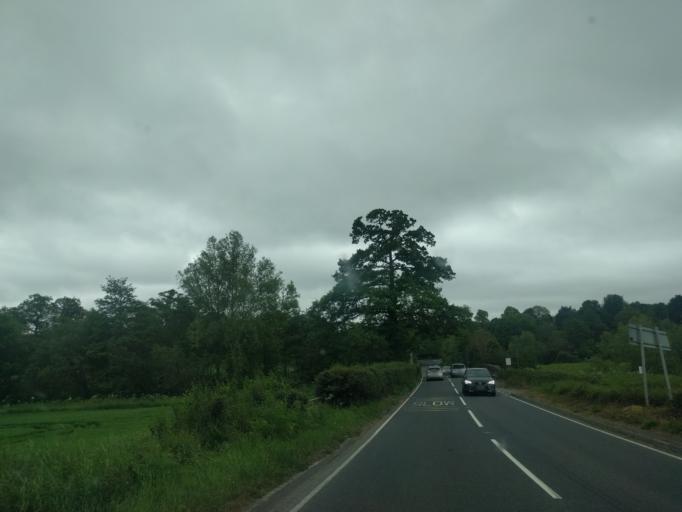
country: GB
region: England
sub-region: Somerset
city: Ilchester
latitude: 51.0584
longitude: -2.7202
